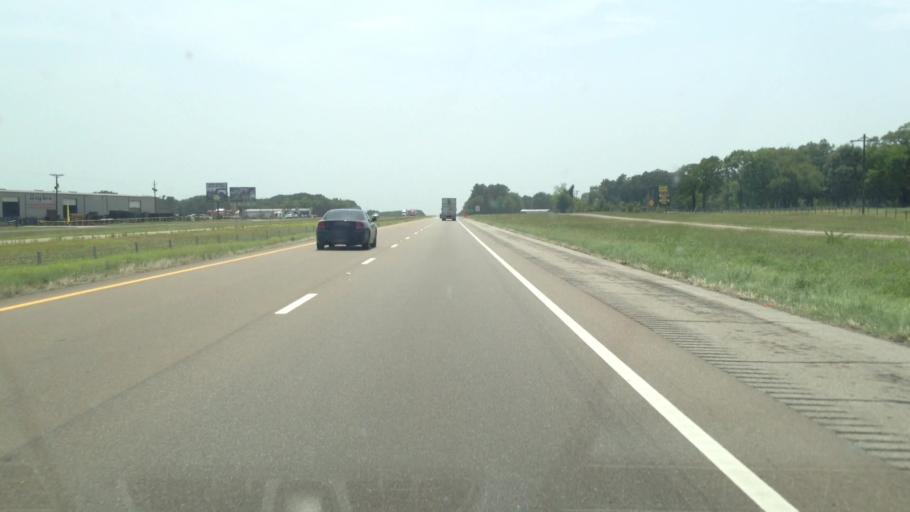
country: US
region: Texas
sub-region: Titus County
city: Mount Pleasant
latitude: 33.1947
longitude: -94.9287
